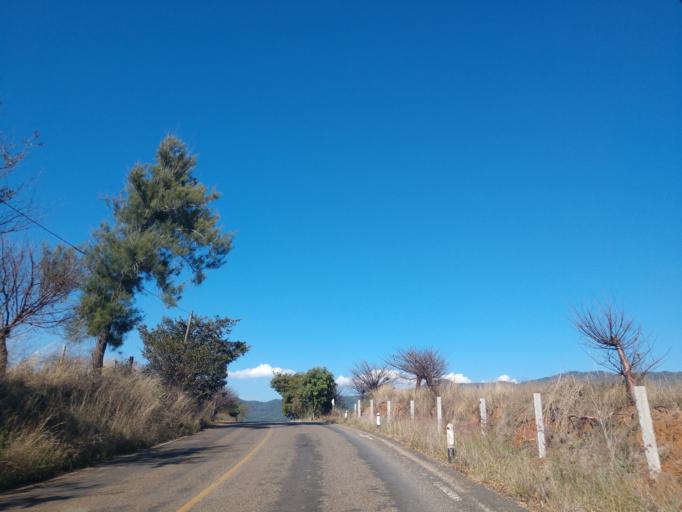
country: MX
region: Nayarit
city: Compostela
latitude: 21.2632
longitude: -104.8938
